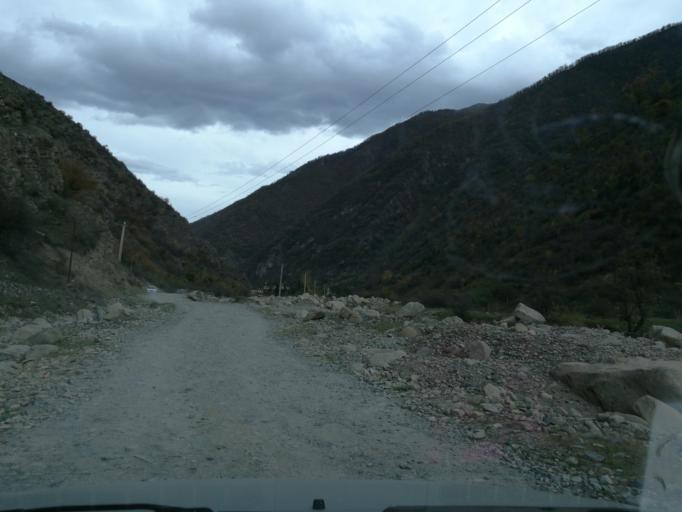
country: IR
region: Mazandaran
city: `Abbasabad
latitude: 36.4497
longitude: 51.0653
